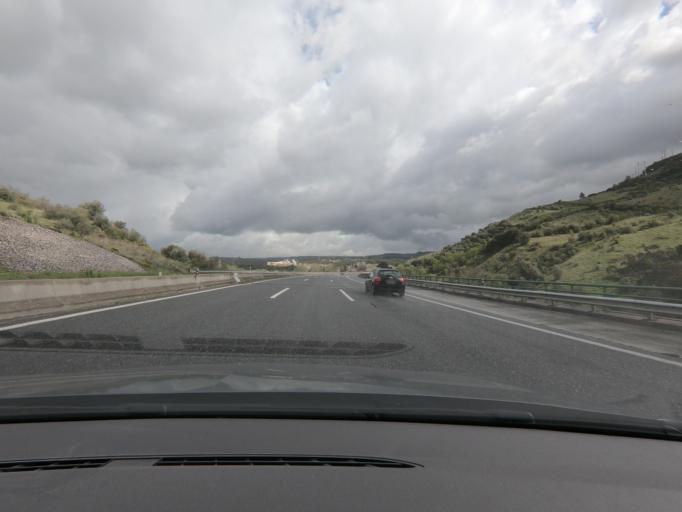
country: PT
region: Lisbon
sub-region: Loures
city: Bucelas
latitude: 38.8897
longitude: -9.1262
